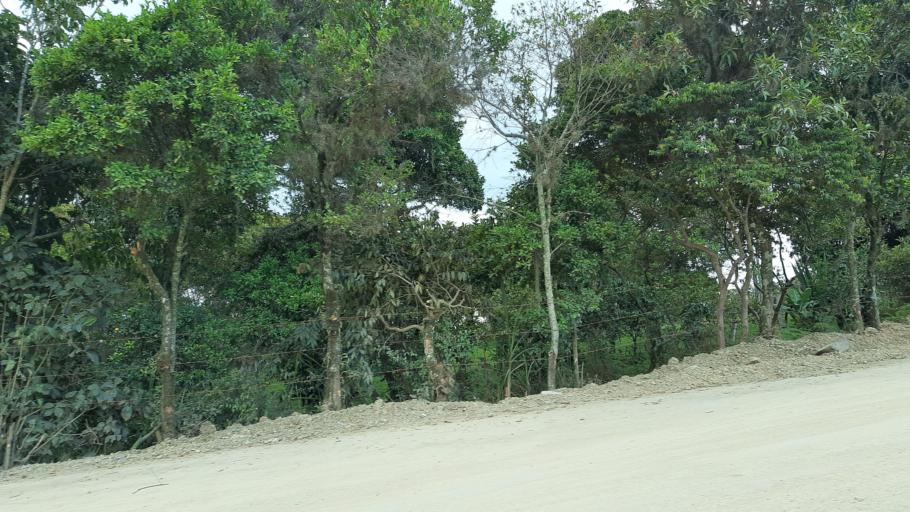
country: CO
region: Boyaca
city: Moniquira
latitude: 5.8086
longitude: -73.5998
